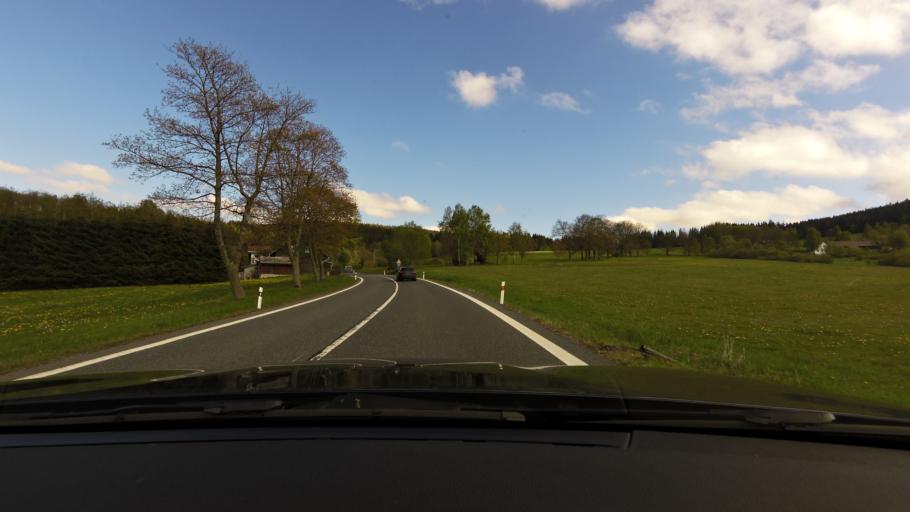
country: CZ
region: Plzensky
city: Strazov
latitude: 49.2177
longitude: 13.2966
